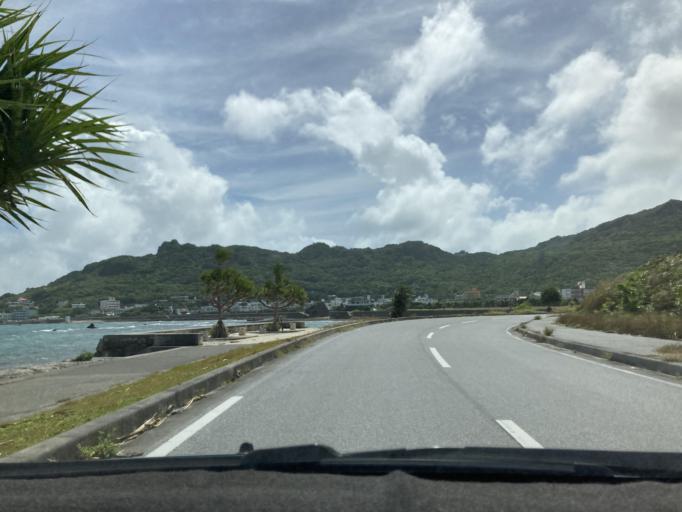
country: JP
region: Okinawa
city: Ginowan
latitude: 26.1843
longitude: 127.8217
